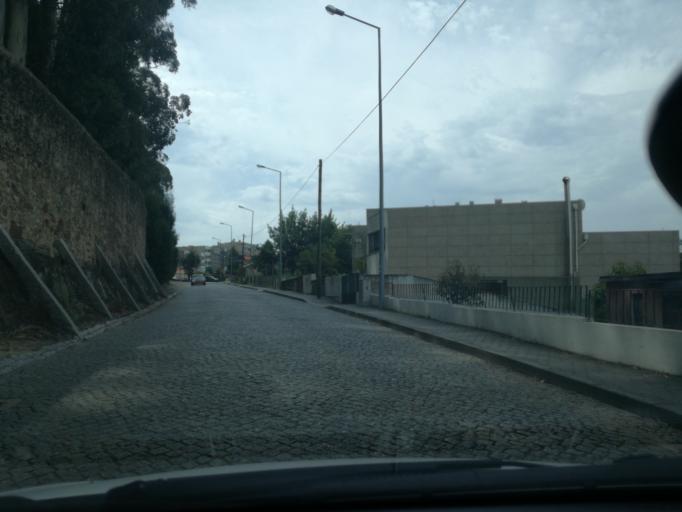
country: PT
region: Porto
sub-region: Vila Nova de Gaia
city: Grijo
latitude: 41.0325
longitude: -8.5886
